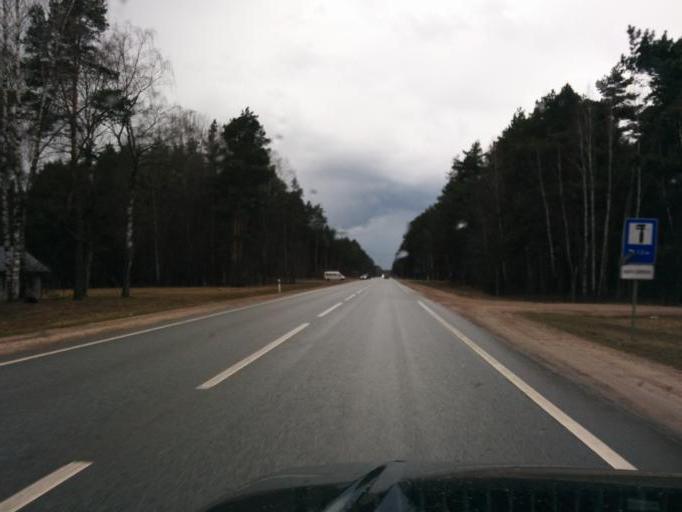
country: LV
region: Babite
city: Pinki
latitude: 56.8847
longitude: 23.9446
